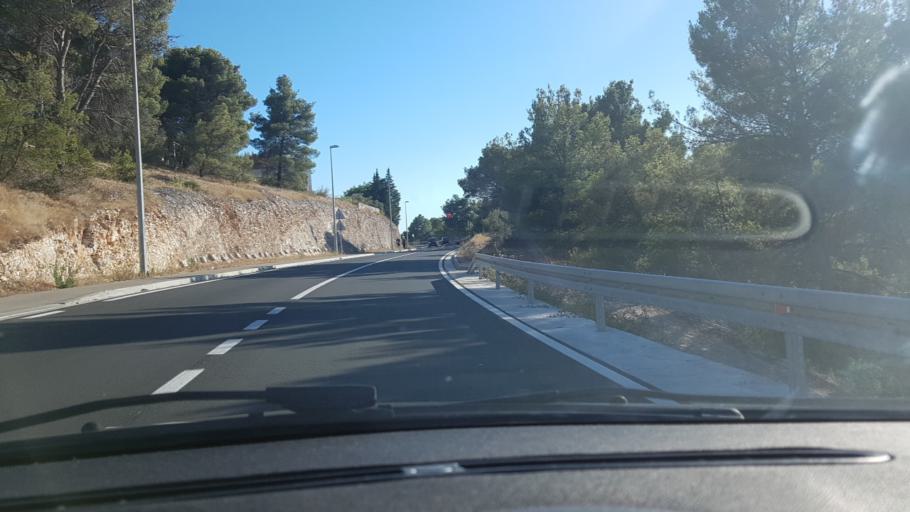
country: HR
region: Sibensko-Kniniska
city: Primosten
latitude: 43.5931
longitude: 15.9258
